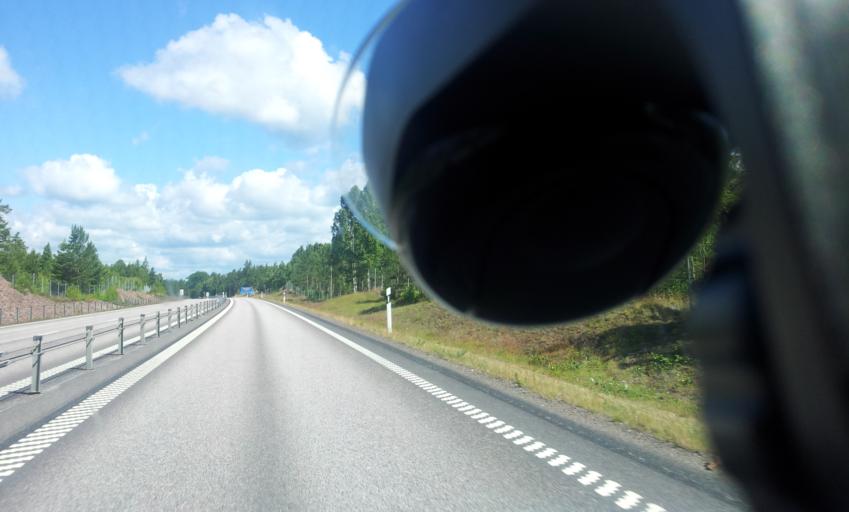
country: SE
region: Kalmar
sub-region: Oskarshamns Kommun
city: Oskarshamn
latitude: 57.2307
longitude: 16.4374
